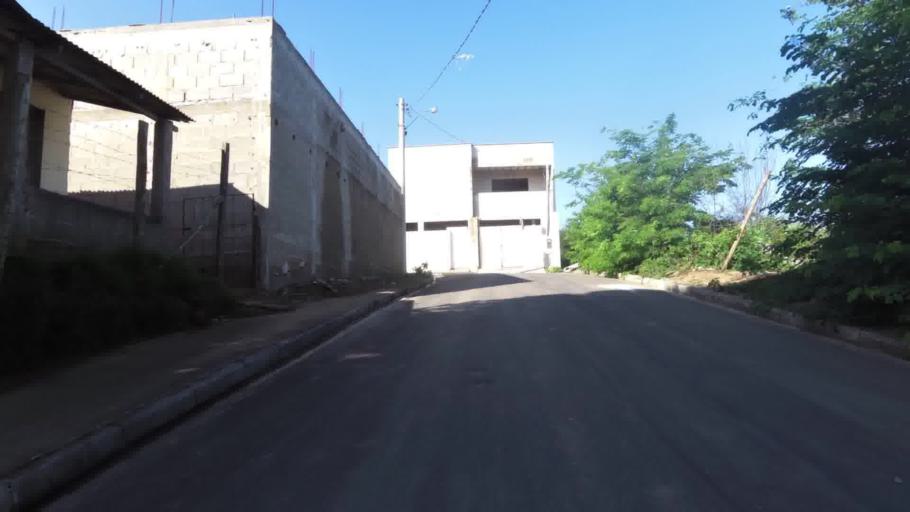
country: BR
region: Espirito Santo
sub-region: Piuma
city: Piuma
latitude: -20.8192
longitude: -40.6241
